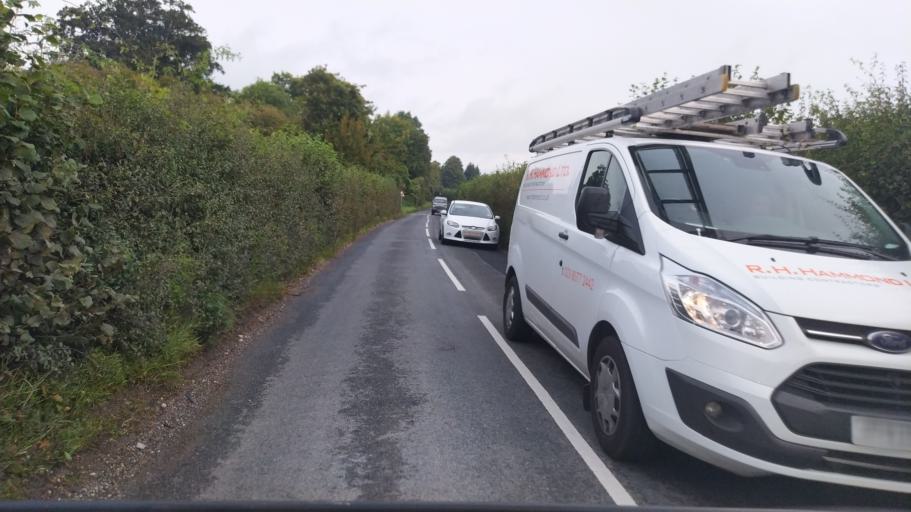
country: GB
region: England
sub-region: Hampshire
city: East Dean
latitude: 51.0651
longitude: -1.5500
